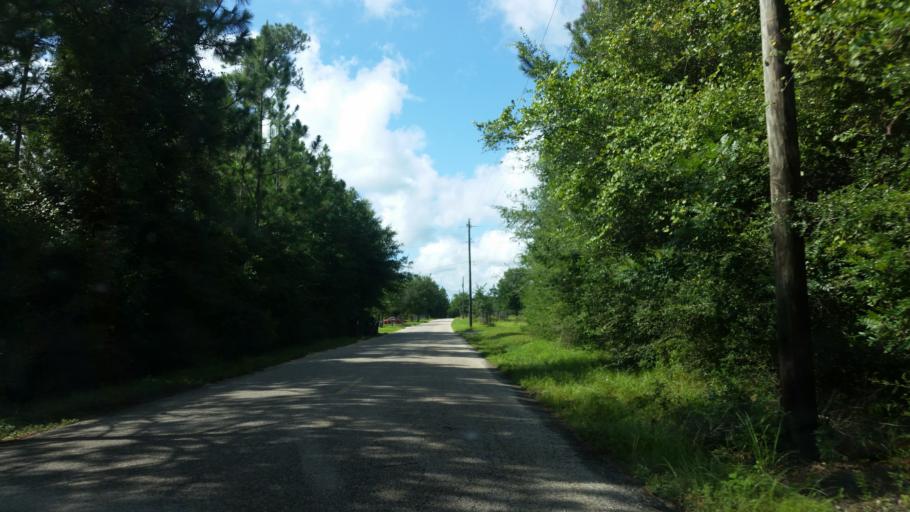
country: US
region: Florida
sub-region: Santa Rosa County
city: Point Baker
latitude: 30.7130
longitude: -86.9555
